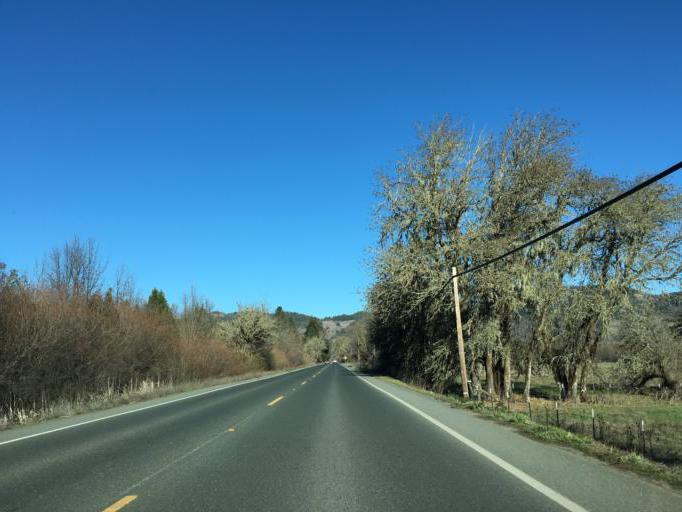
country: US
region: California
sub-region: Mendocino County
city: Brooktrails
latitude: 39.4431
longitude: -123.3536
